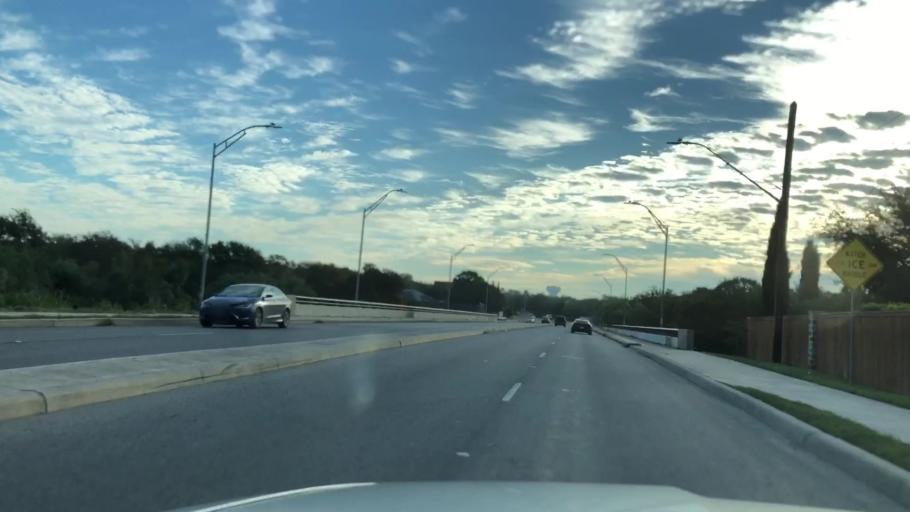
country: US
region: Texas
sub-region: Bexar County
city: Leon Valley
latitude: 29.5415
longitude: -98.6328
